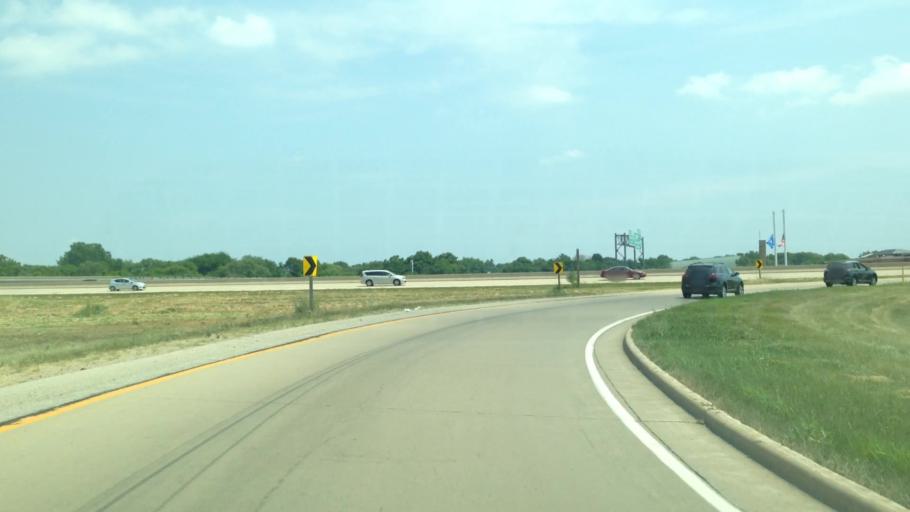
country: US
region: Wisconsin
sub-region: Dane County
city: Middleton
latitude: 43.0986
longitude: -89.5173
